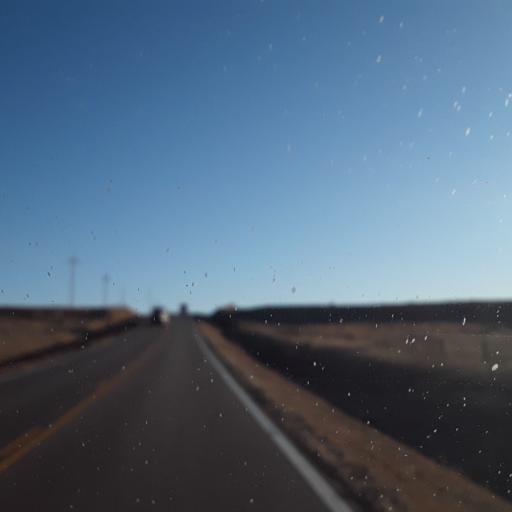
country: US
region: Kansas
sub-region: Wallace County
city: Sharon Springs
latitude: 38.9917
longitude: -101.7392
